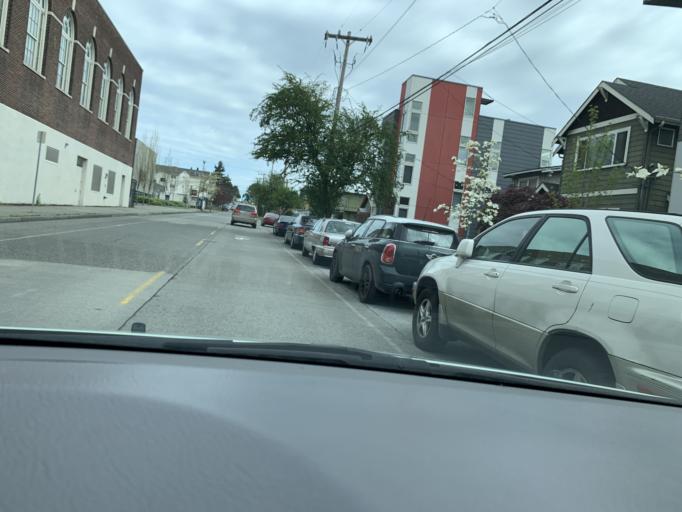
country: US
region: Washington
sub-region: King County
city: White Center
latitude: 47.5521
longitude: -122.3135
